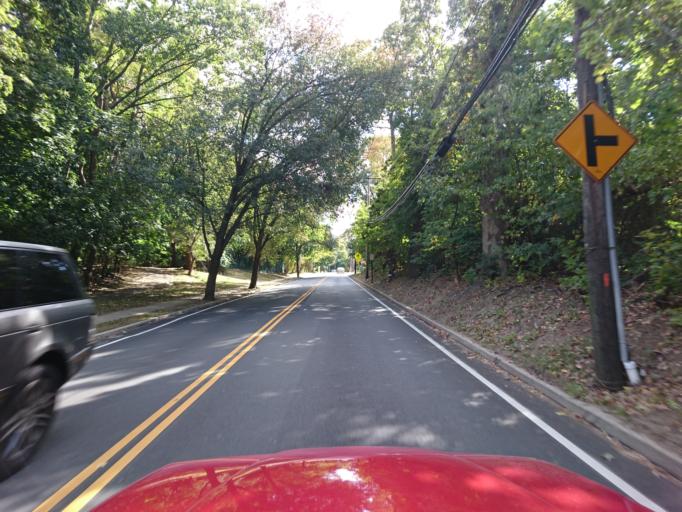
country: US
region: New York
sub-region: Nassau County
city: Glen Cove
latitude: 40.8802
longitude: -73.6300
